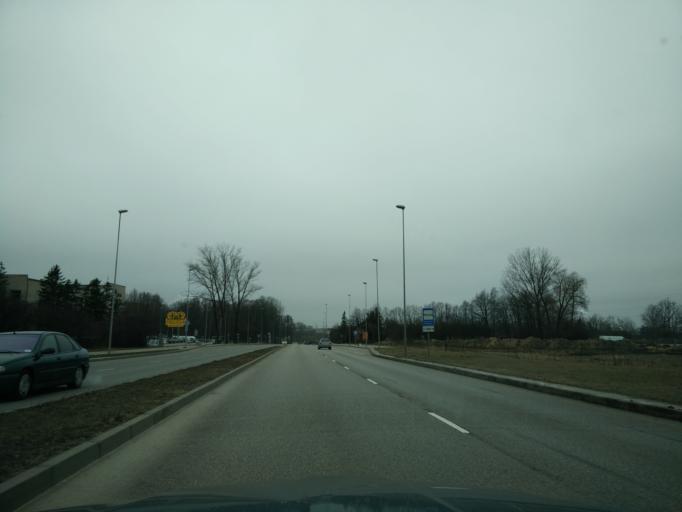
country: LT
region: Klaipedos apskritis
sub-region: Klaipeda
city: Klaipeda
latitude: 55.7281
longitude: 21.1747
